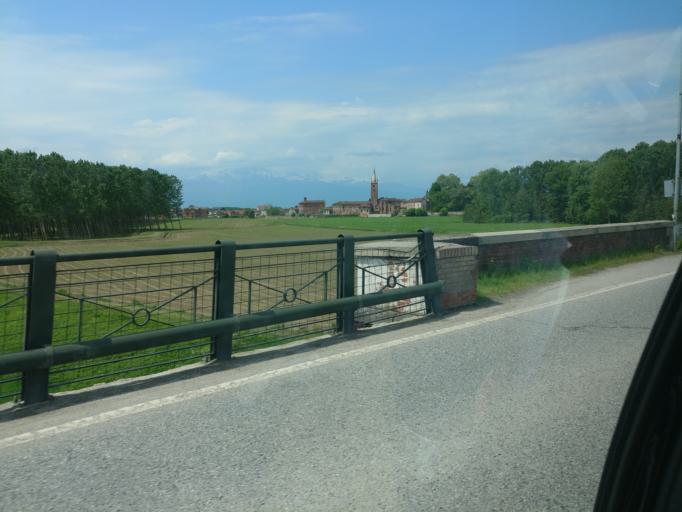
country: IT
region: Piedmont
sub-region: Provincia di Torino
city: Villafranca Piemonte
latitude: 44.7799
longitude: 7.5120
